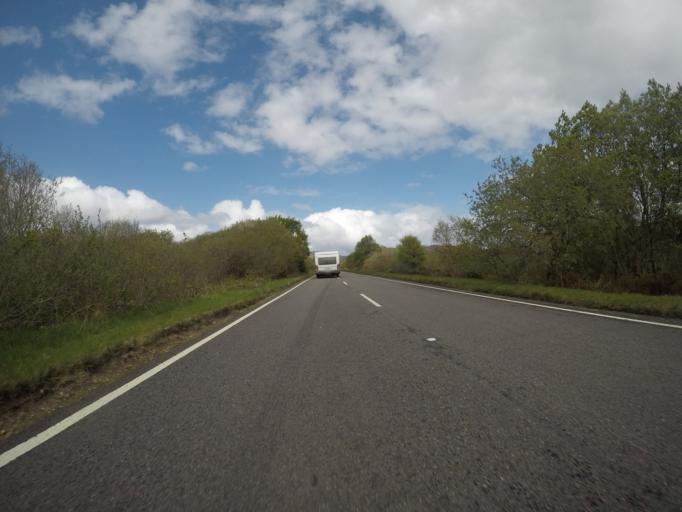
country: GB
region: Scotland
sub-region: Highland
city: Portree
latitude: 57.2529
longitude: -5.9371
